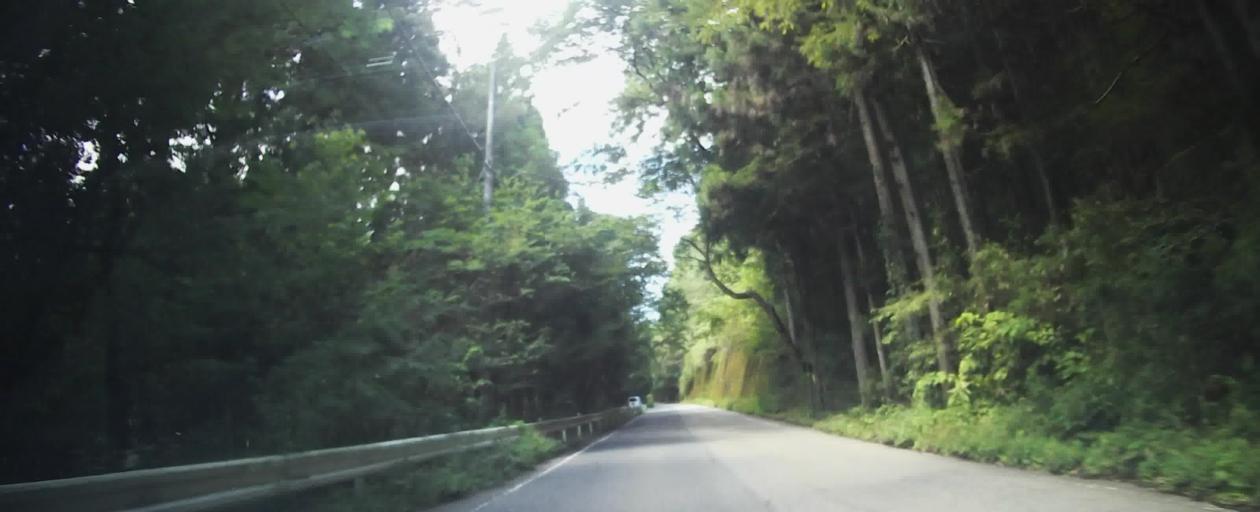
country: JP
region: Gunma
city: Kanekomachi
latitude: 36.4400
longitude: 138.9125
